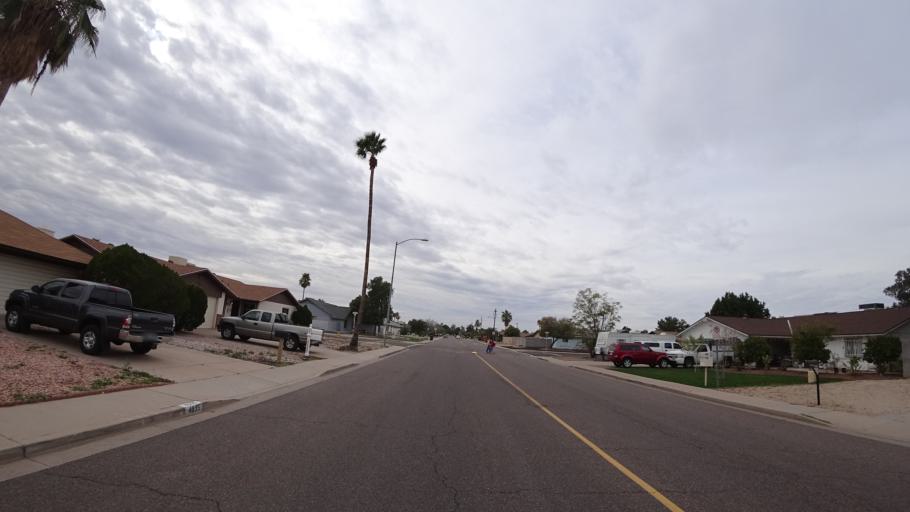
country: US
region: Arizona
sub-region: Maricopa County
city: Peoria
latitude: 33.6473
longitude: -112.1470
